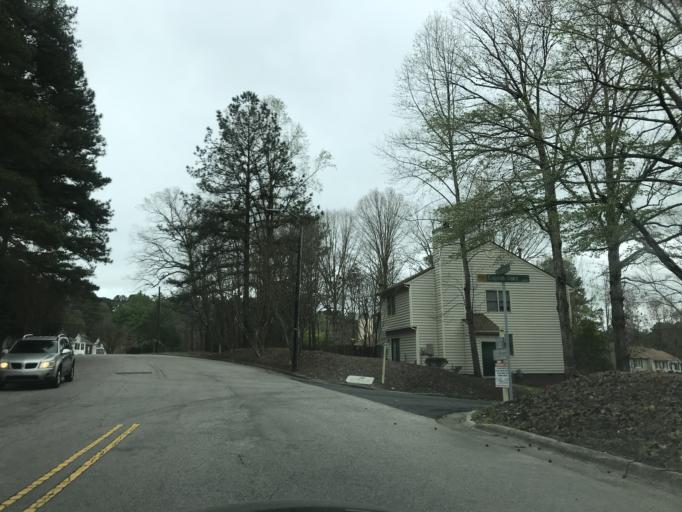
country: US
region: North Carolina
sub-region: Wake County
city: West Raleigh
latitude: 35.8702
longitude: -78.6489
